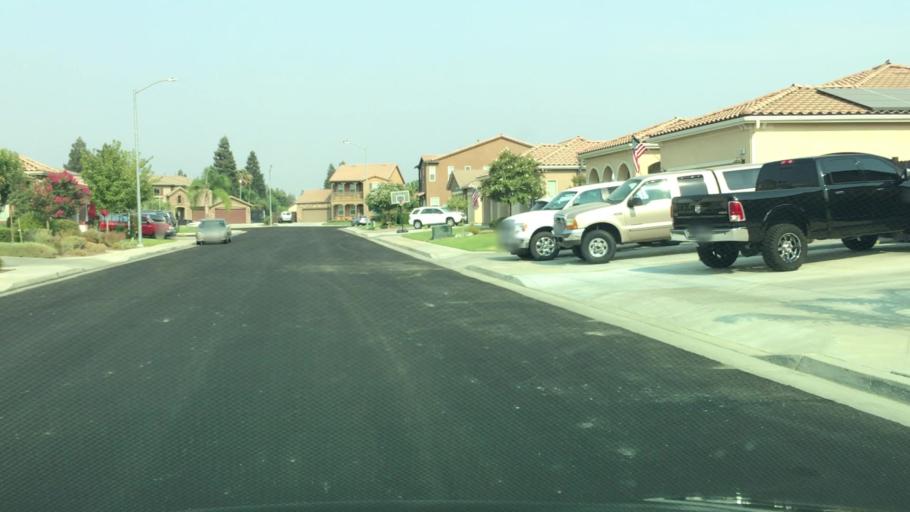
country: US
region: California
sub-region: Fresno County
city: Tarpey Village
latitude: 36.7929
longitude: -119.6751
